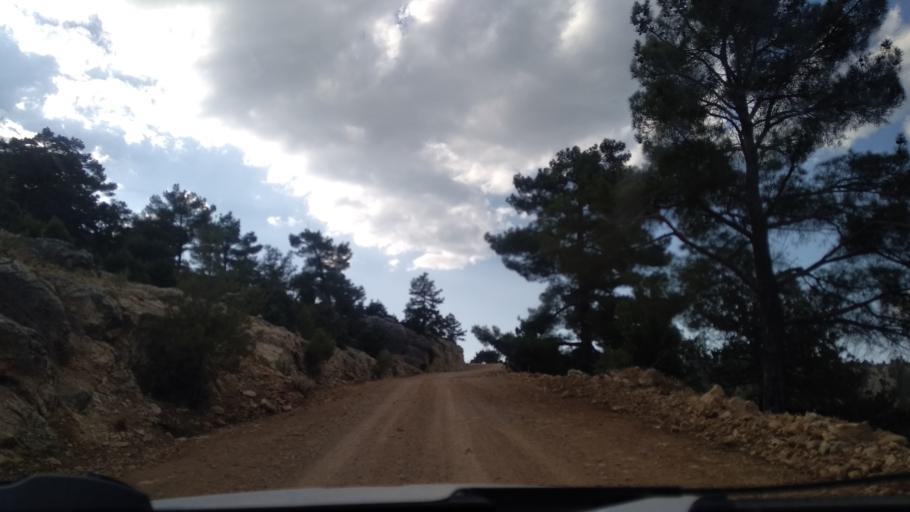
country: TR
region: Mersin
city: Sarikavak
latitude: 36.5988
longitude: 33.7034
